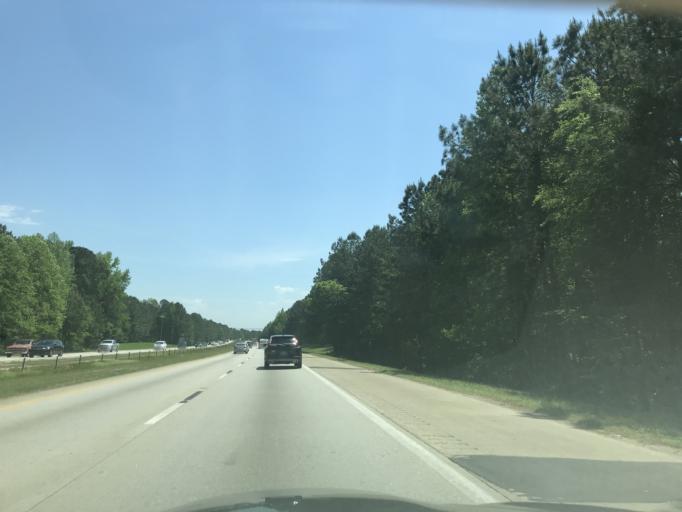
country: US
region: North Carolina
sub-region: Wake County
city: Garner
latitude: 35.6850
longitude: -78.5697
